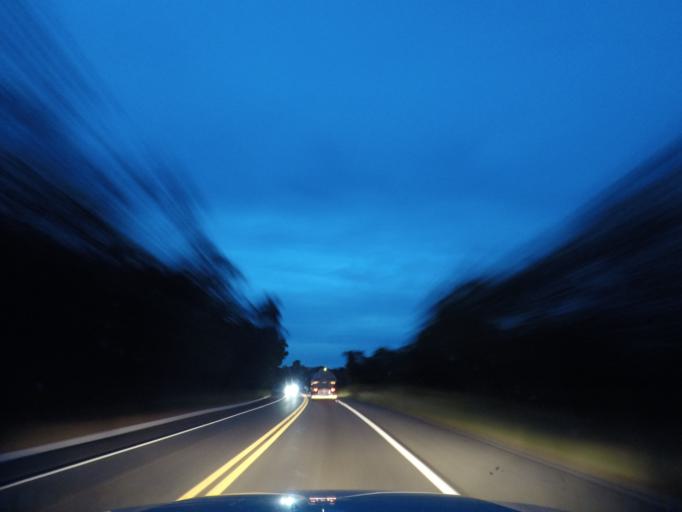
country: BR
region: Bahia
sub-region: Andarai
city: Vera Cruz
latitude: -12.4840
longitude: -41.3467
